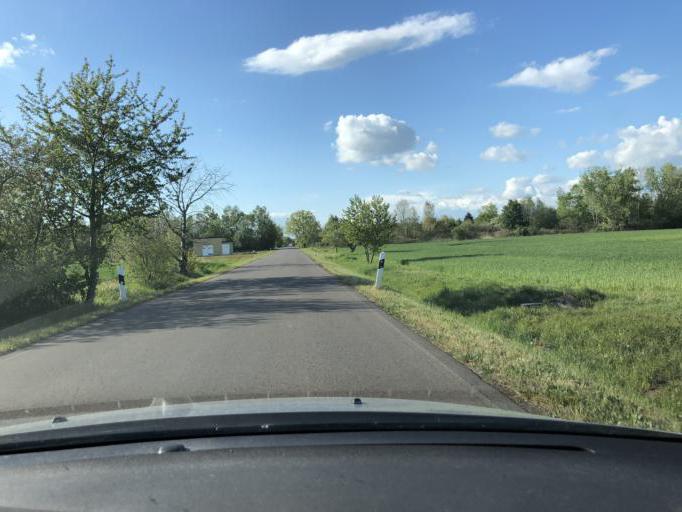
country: DE
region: Saxony
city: Deutzen
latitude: 51.1246
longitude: 12.4568
